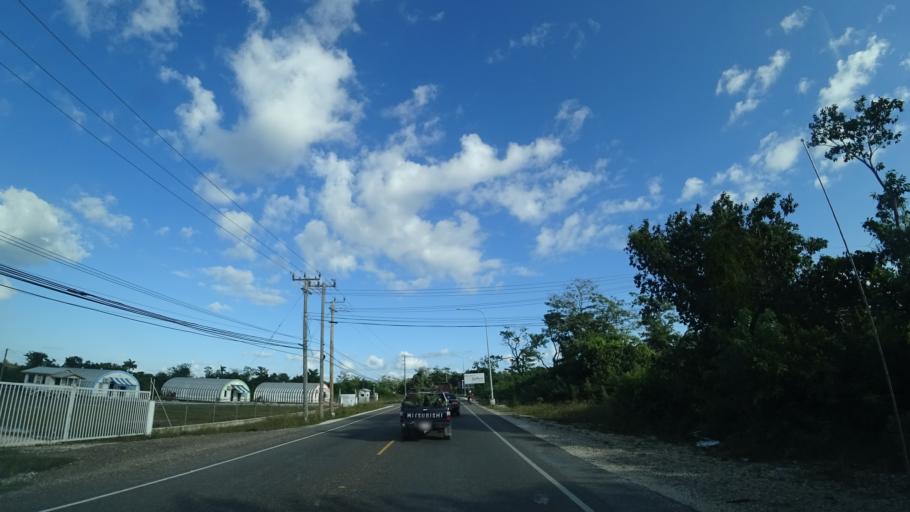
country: BZ
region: Belize
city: Belize City
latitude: 17.5455
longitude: -88.2855
